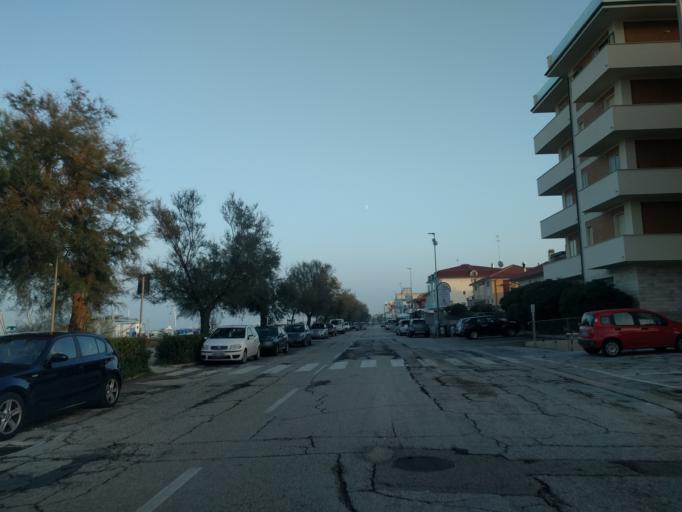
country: IT
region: The Marches
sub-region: Provincia di Ancona
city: Senigallia
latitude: 43.7288
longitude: 13.2033
